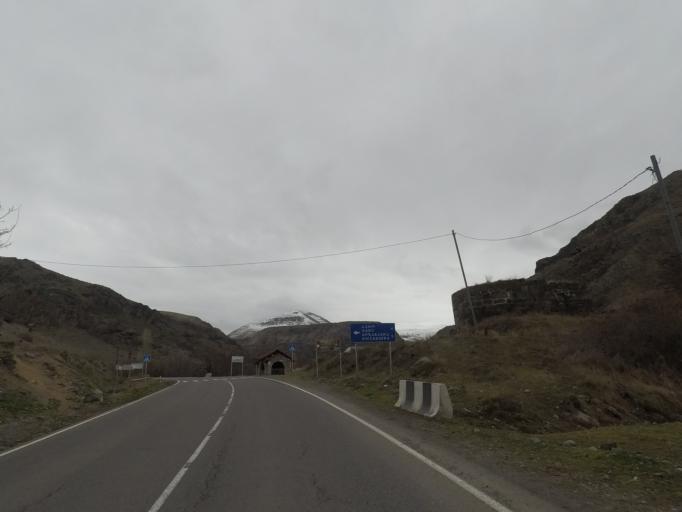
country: GE
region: Samtskhe-Javakheti
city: Aspindza
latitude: 41.4978
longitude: 43.2634
